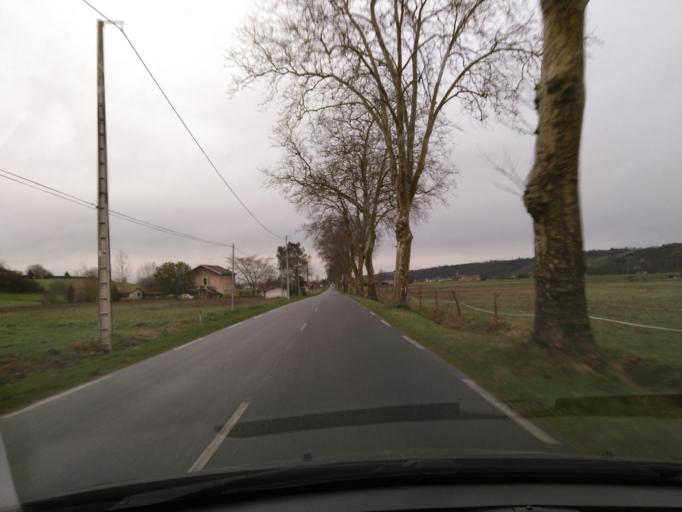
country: FR
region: Midi-Pyrenees
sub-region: Departement de la Haute-Garonne
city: Montesquieu-Volvestre
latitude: 43.1898
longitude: 1.2373
